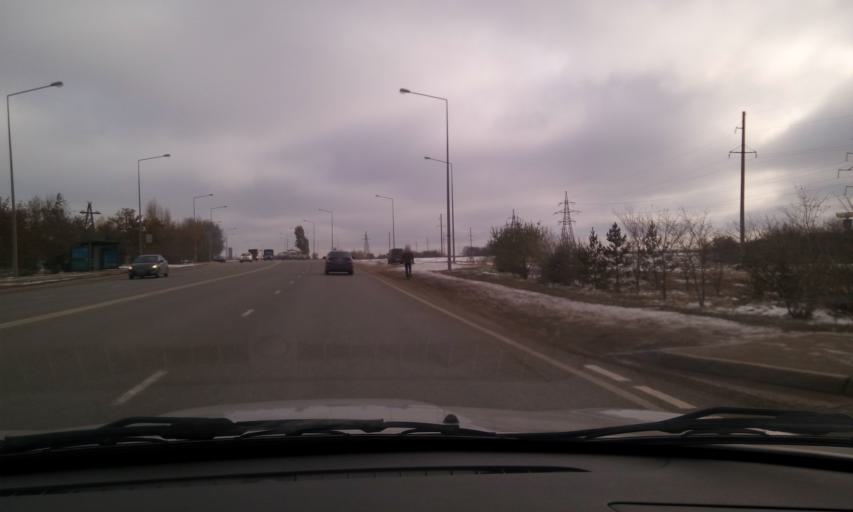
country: KZ
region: Astana Qalasy
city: Astana
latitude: 51.1359
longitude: 71.5388
